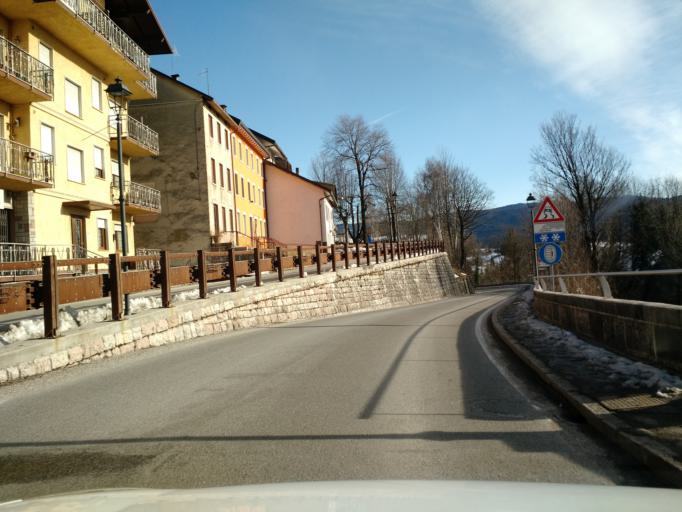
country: IT
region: Veneto
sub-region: Provincia di Vicenza
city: Roana
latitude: 45.8750
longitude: 11.4639
